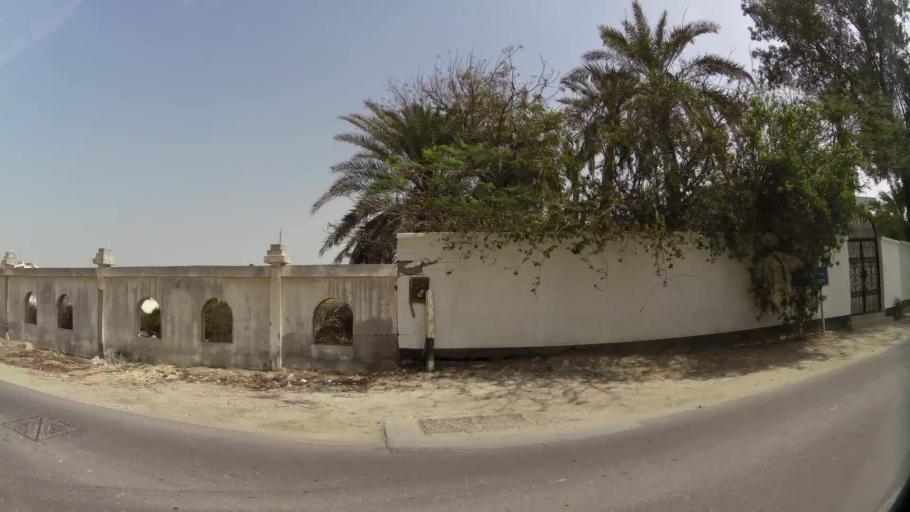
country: BH
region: Manama
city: Jidd Hafs
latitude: 26.2216
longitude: 50.4843
